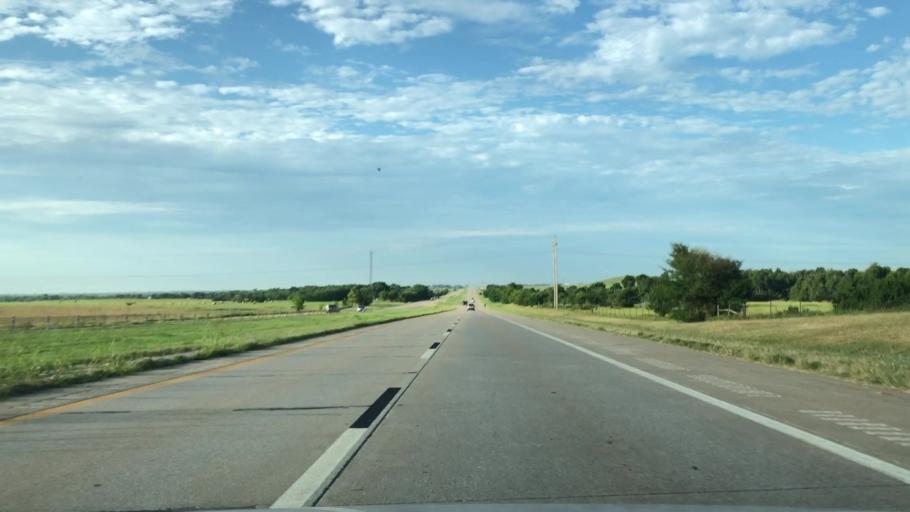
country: US
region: Oklahoma
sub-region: Osage County
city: Skiatook
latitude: 36.4054
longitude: -95.9206
